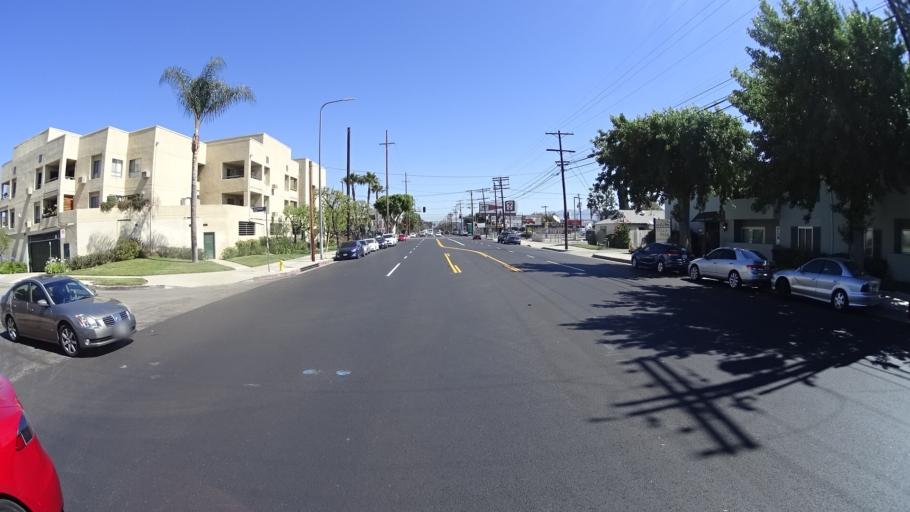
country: US
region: California
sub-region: Los Angeles County
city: Van Nuys
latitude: 34.1928
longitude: -118.4924
